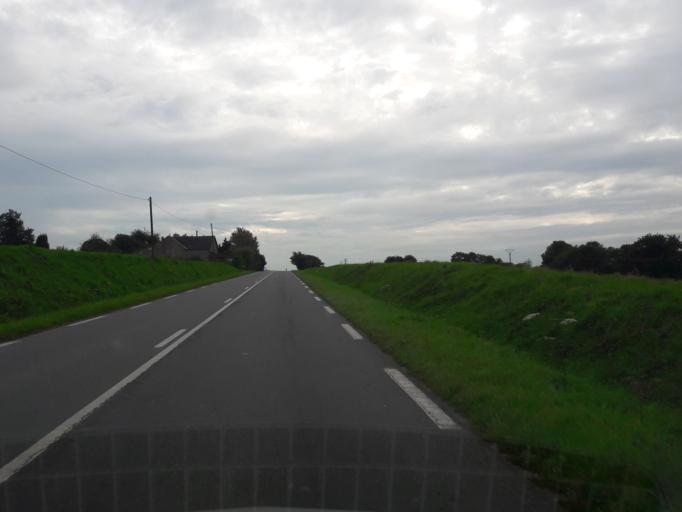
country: FR
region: Lower Normandy
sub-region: Departement du Calvados
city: Cahagnes
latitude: 49.1274
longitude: -0.7444
